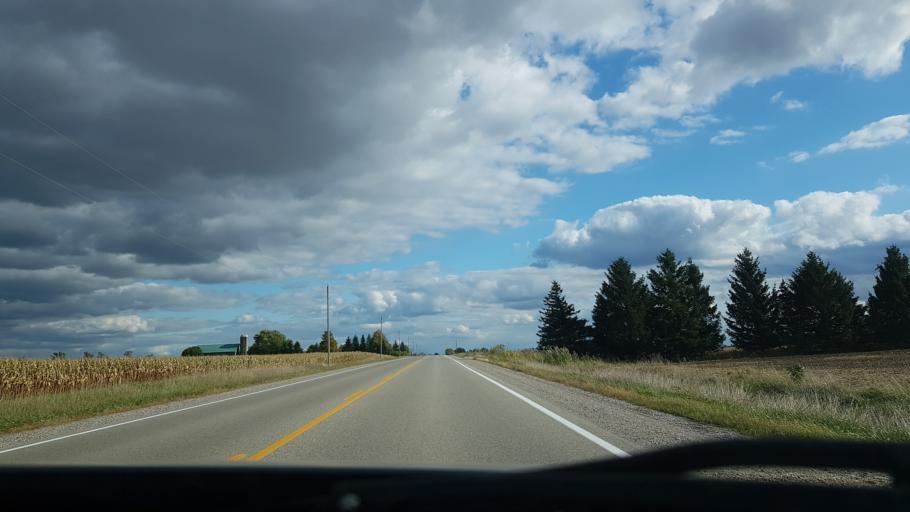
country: CA
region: Ontario
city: Delaware
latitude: 43.0597
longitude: -81.5029
